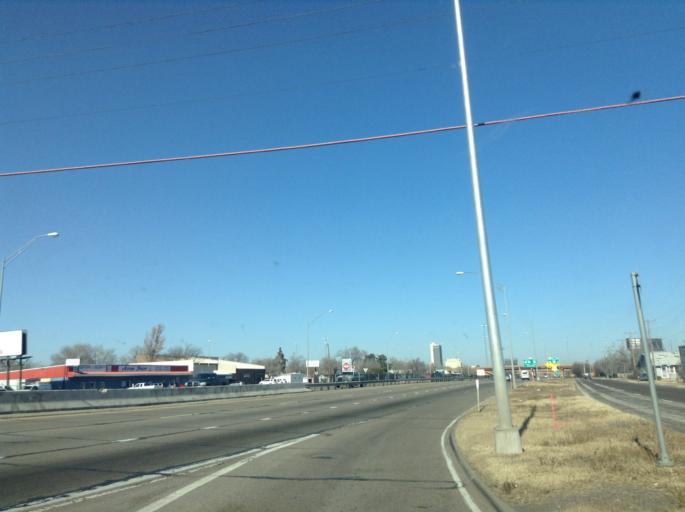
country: US
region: Texas
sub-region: Potter County
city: Amarillo
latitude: 35.1873
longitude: -101.8380
